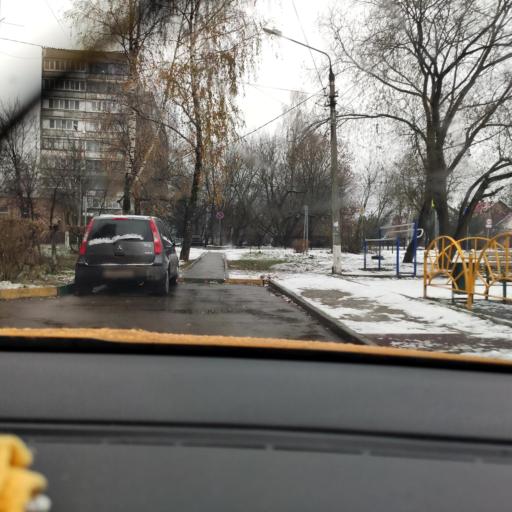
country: RU
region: Moskovskaya
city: Domodedovo
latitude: 55.4499
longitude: 37.7532
